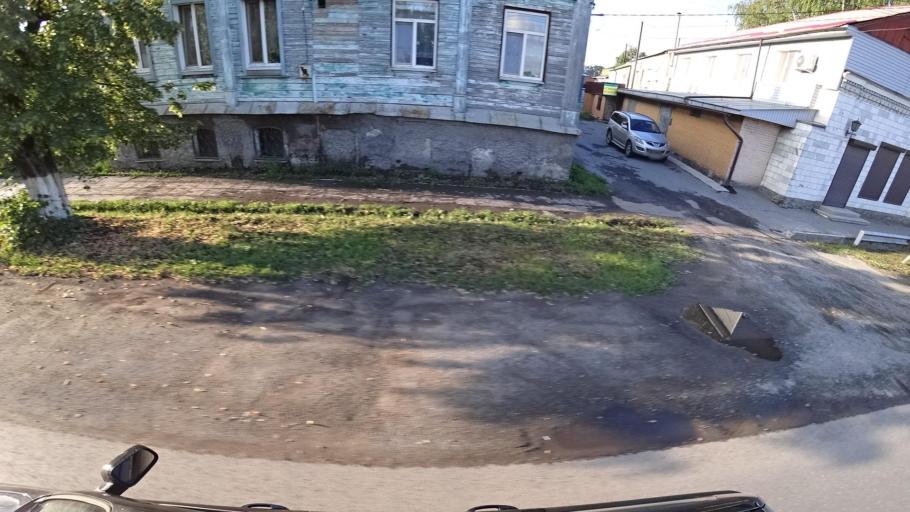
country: RU
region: Sverdlovsk
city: Kamyshlov
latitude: 56.8471
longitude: 62.7079
